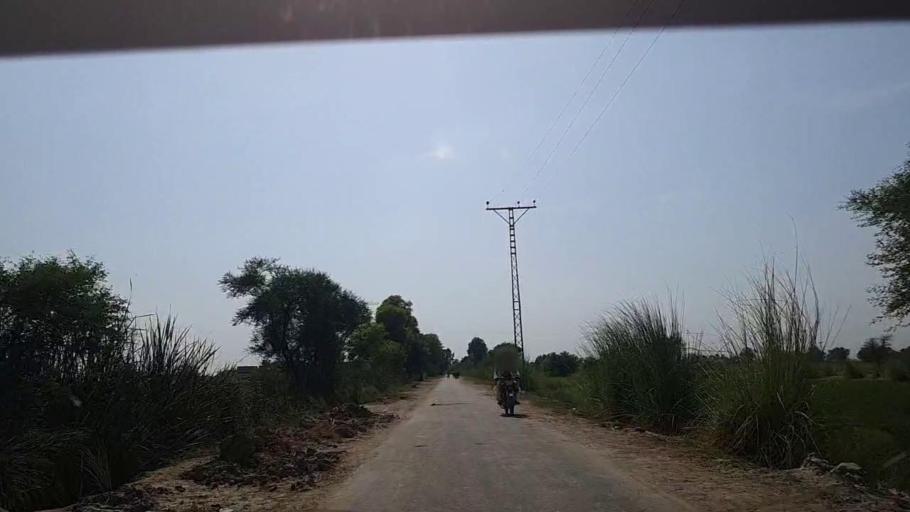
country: PK
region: Sindh
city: Khanpur
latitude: 27.8442
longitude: 69.3979
